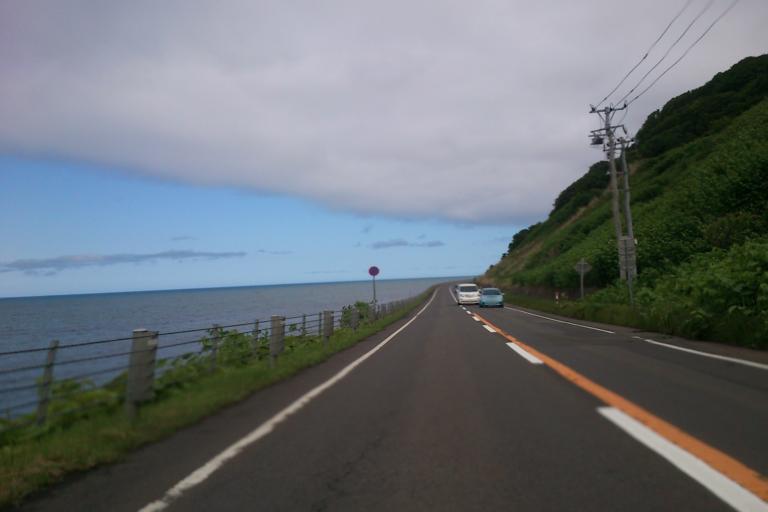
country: JP
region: Hokkaido
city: Ishikari
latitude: 43.4245
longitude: 141.4253
